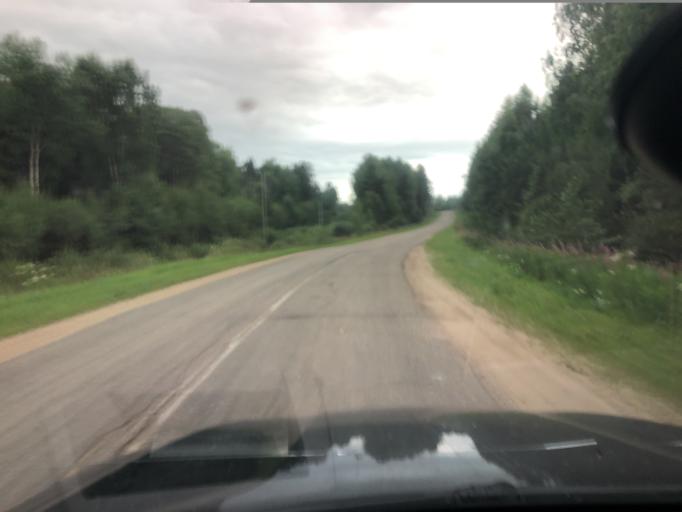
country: RU
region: Jaroslavl
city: Pereslavl'-Zalesskiy
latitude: 57.0359
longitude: 38.9060
